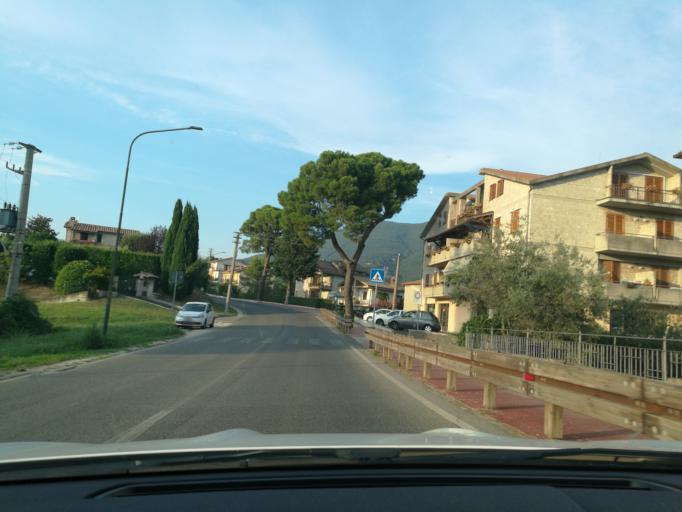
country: IT
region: Umbria
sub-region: Provincia di Terni
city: San Gemini
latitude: 42.6174
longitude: 12.5497
